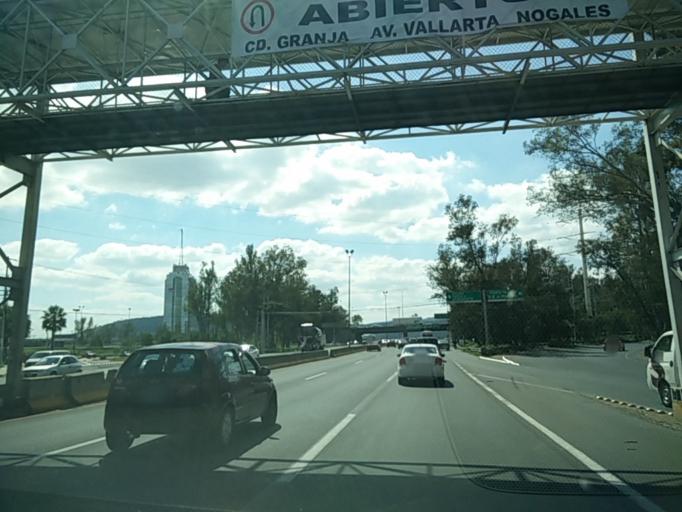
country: MX
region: Jalisco
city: Zapopan2
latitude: 20.6978
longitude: -103.4536
